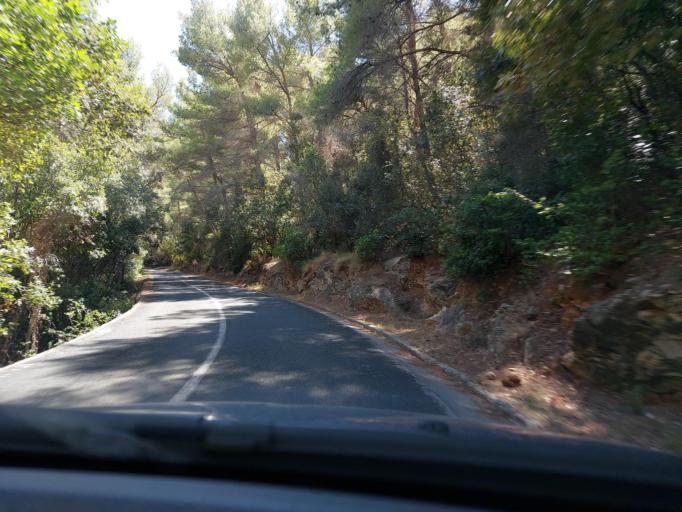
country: HR
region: Dubrovacko-Neretvanska
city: Smokvica
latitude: 42.7679
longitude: 16.8857
